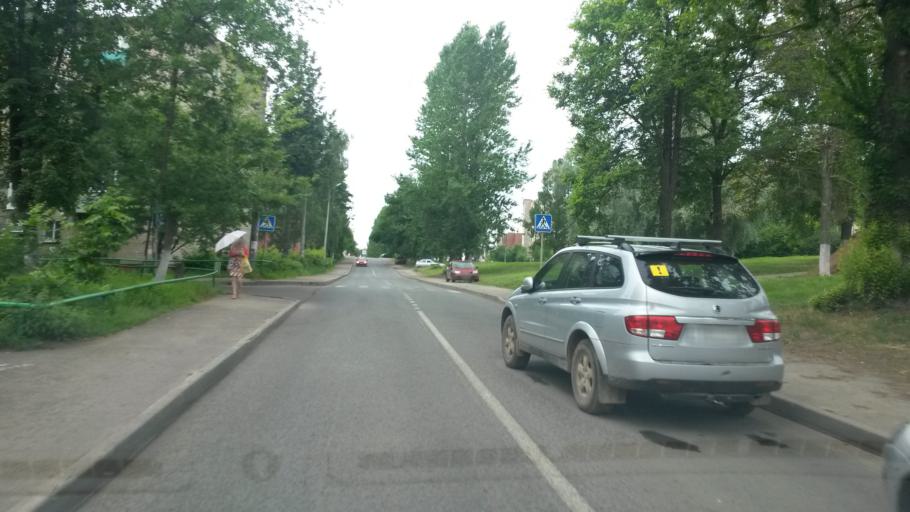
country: RU
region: Jaroslavl
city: Yaroslavl
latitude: 57.5835
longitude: 39.8628
